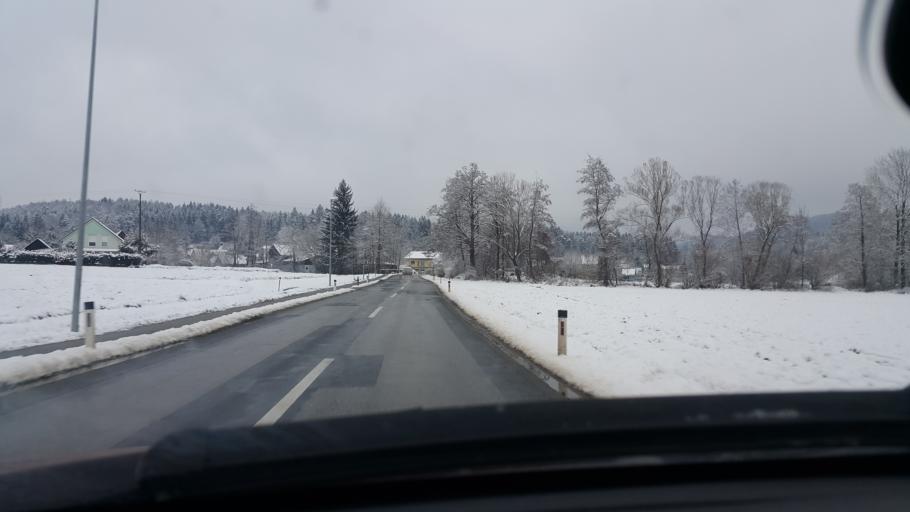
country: AT
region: Styria
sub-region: Politischer Bezirk Graz-Umgebung
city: Hitzendorf
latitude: 47.0597
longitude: 15.2923
